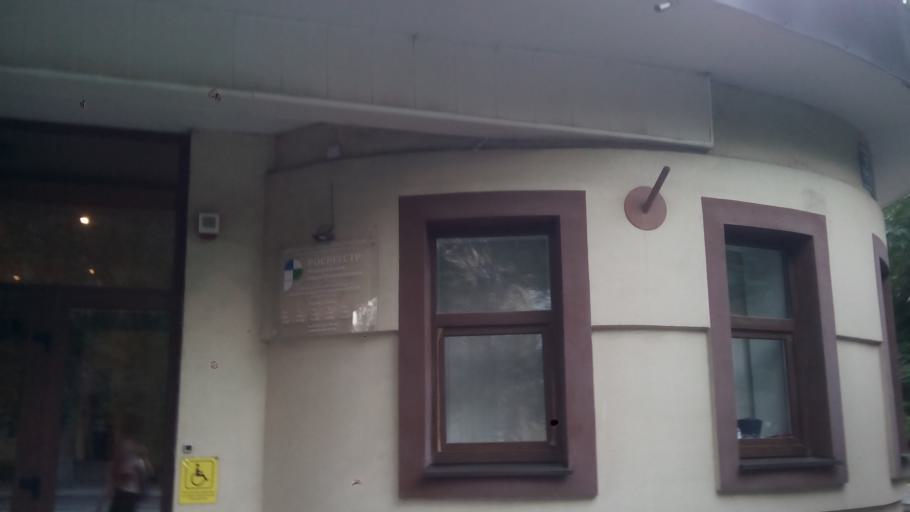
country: RU
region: Rostov
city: Imeni Chkalova
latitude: 47.2509
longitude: 39.7691
